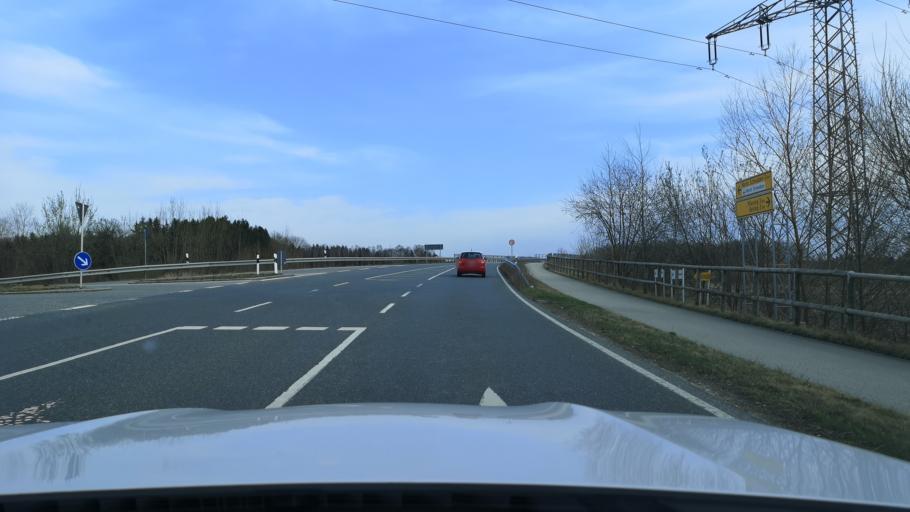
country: DE
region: Bavaria
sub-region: Upper Bavaria
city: Finsing
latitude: 48.1977
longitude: 11.8331
